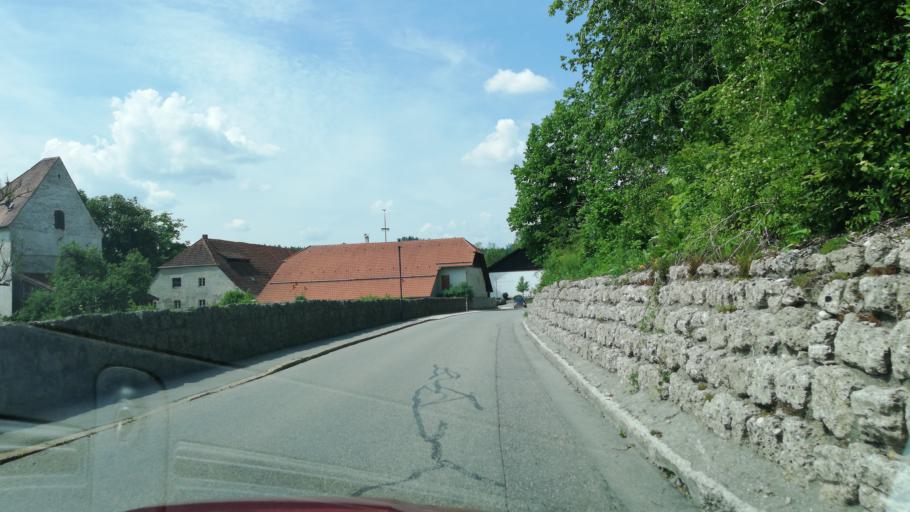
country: DE
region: Bavaria
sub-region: Upper Bavaria
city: Mehring
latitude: 48.1297
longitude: 12.7877
